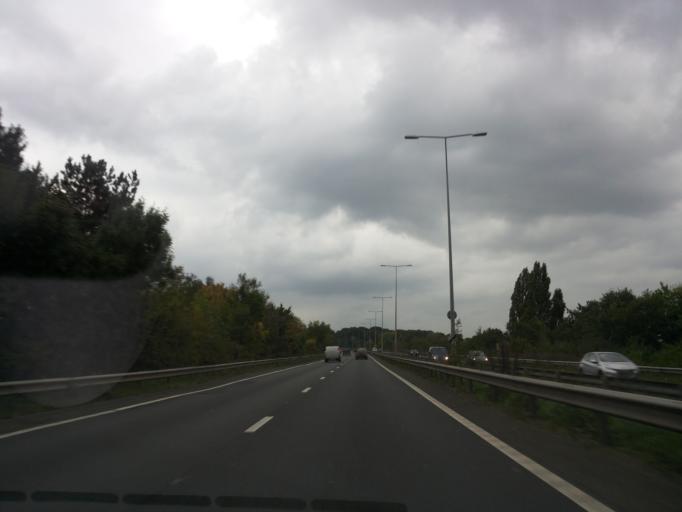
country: GB
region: England
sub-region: Kent
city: Dunkirk
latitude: 51.2936
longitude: 0.9532
